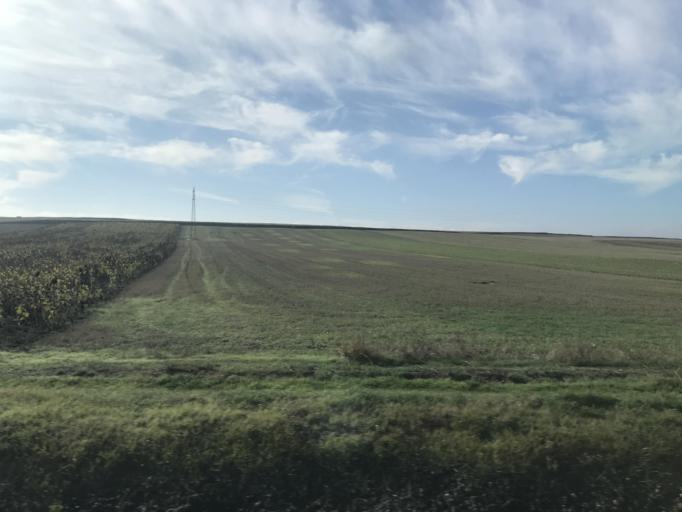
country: ES
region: Castille and Leon
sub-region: Provincia de Burgos
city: Fuentebureba
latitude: 42.6244
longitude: -3.2251
